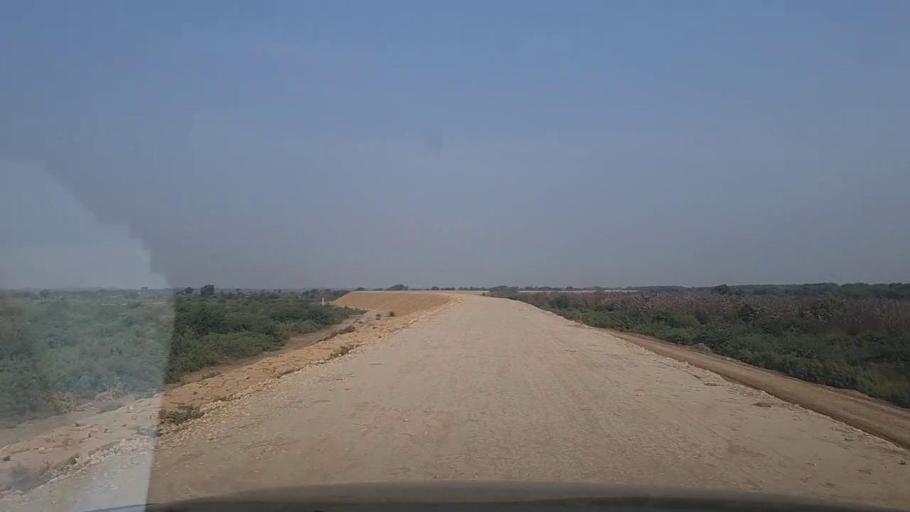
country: PK
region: Sindh
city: Bulri
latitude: 24.9649
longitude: 68.2913
